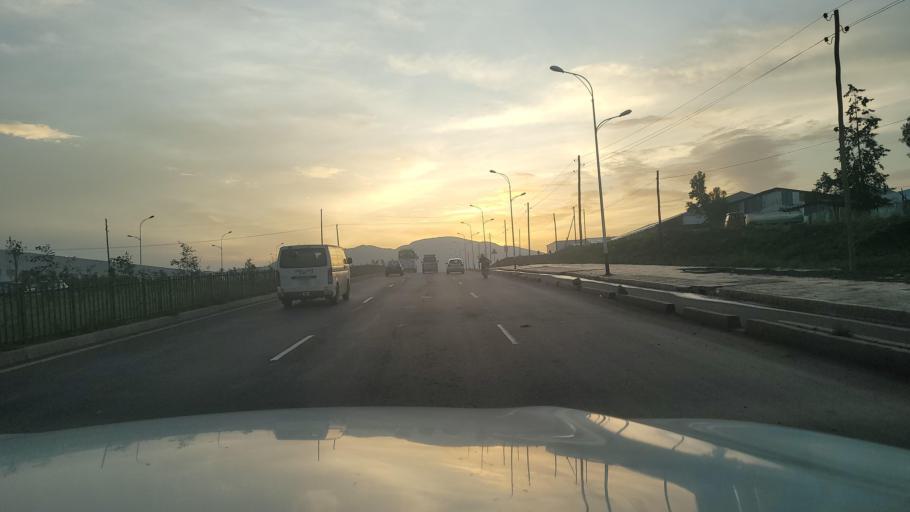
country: ET
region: Adis Abeba
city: Addis Ababa
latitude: 8.9489
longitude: 38.7083
